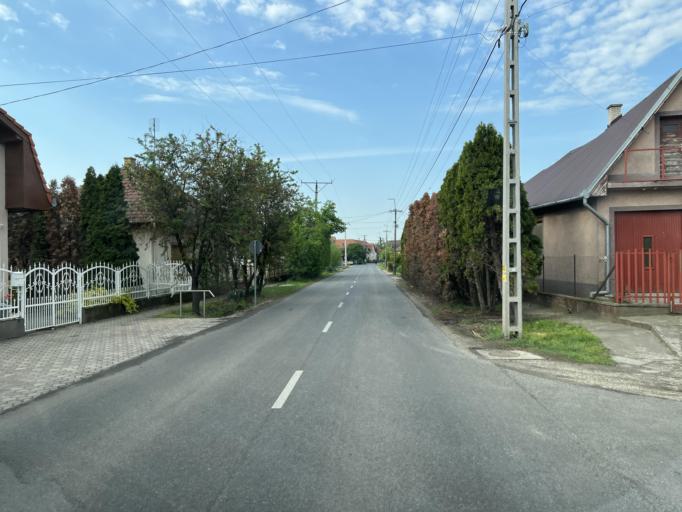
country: HU
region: Pest
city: Abony
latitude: 47.1928
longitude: 20.0106
